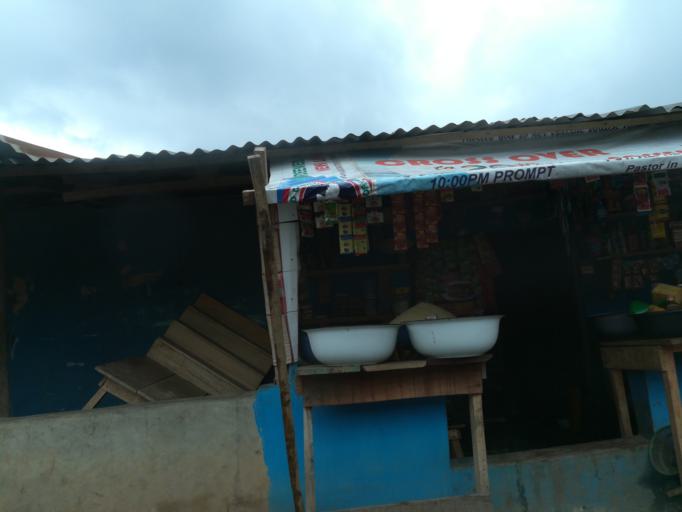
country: NG
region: Lagos
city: Agege
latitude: 6.6049
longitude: 3.3070
